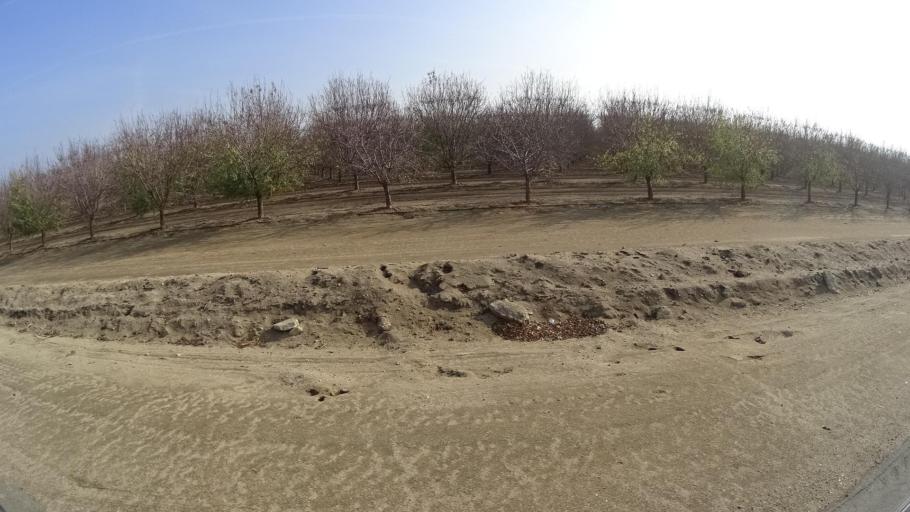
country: US
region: California
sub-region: Kern County
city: Lebec
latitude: 35.0011
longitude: -118.8466
